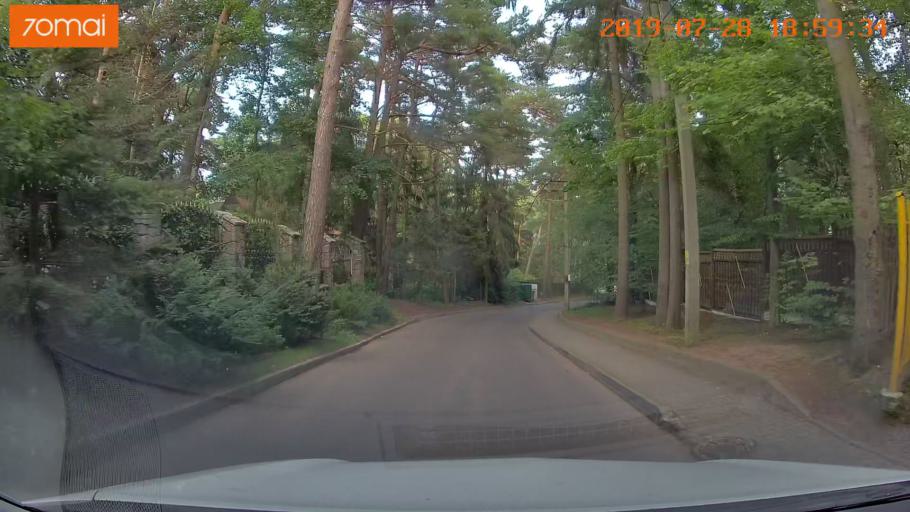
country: RU
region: Kaliningrad
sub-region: Gorod Svetlogorsk
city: Svetlogorsk
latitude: 54.9407
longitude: 20.1601
